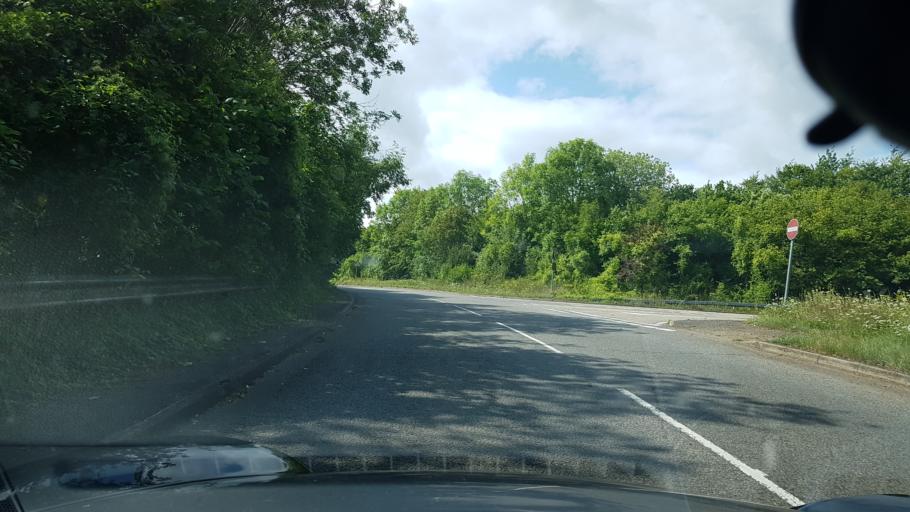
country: GB
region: England
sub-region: Surrey
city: Seale
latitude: 51.2250
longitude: -0.7238
